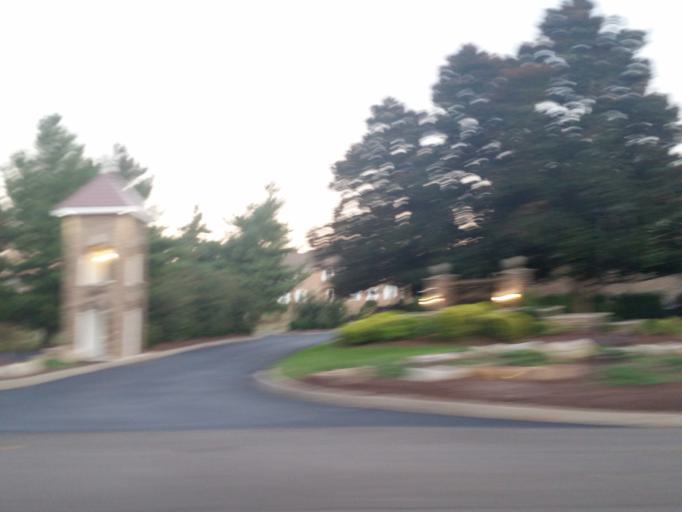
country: US
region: Tennessee
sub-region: Knox County
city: Knoxville
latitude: 36.0577
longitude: -83.8916
